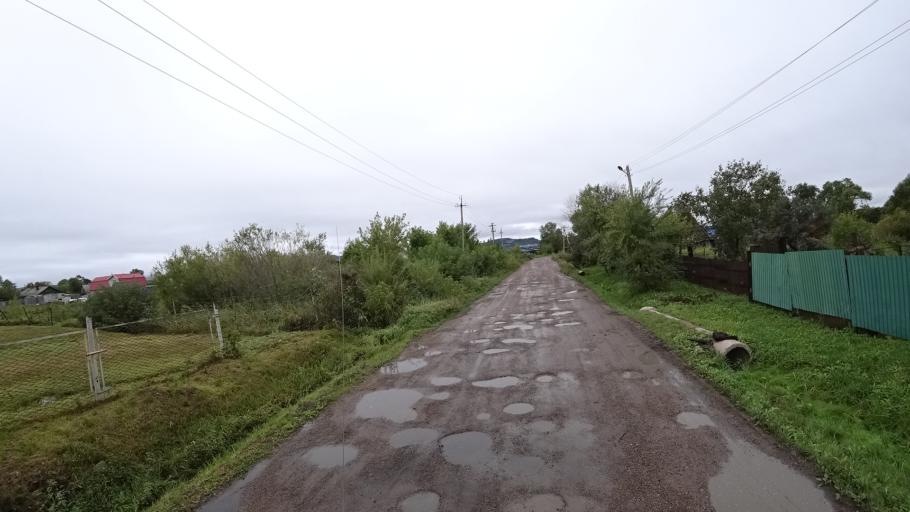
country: RU
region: Primorskiy
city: Monastyrishche
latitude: 44.1971
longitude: 132.4617
